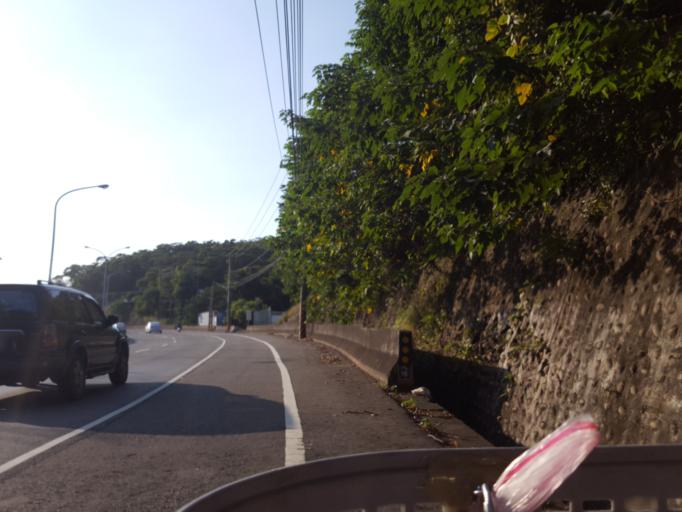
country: TW
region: Taiwan
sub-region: Hsinchu
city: Zhubei
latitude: 24.8589
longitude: 120.9965
